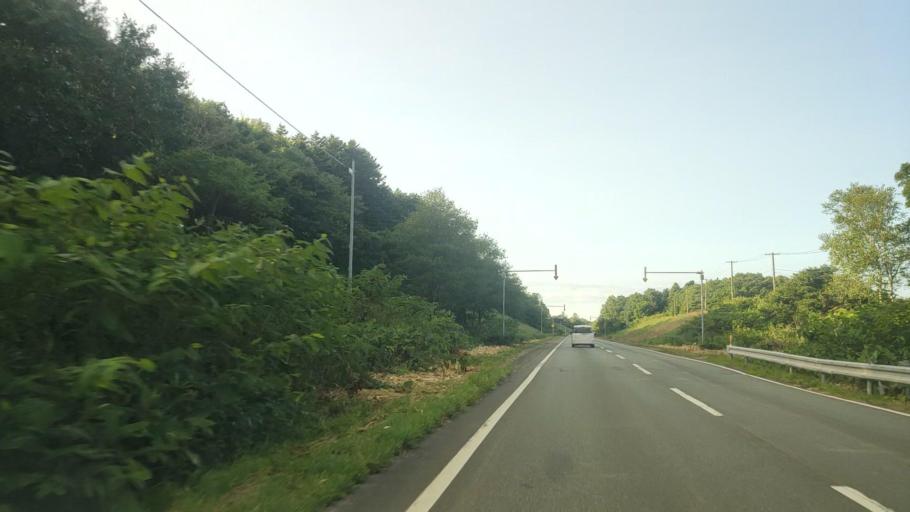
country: JP
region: Hokkaido
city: Makubetsu
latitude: 45.0631
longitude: 141.7483
